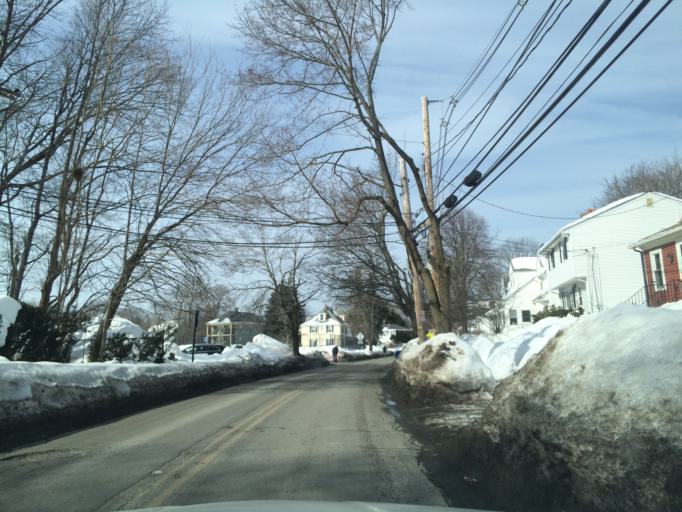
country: US
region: Massachusetts
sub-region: Norfolk County
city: Needham
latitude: 42.3094
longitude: -71.2232
